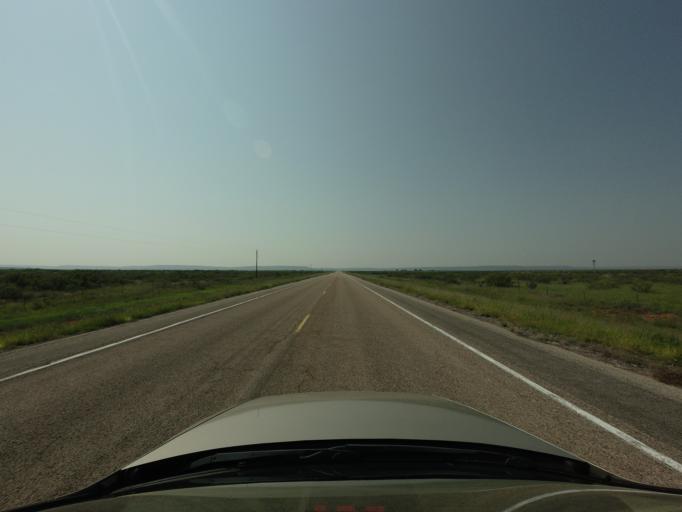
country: US
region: New Mexico
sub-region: Quay County
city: Tucumcari
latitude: 34.9185
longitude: -103.7602
